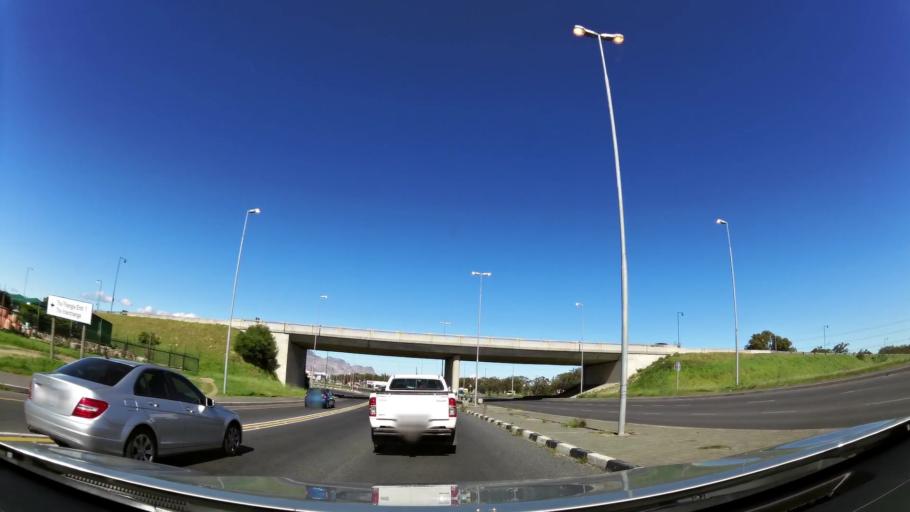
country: ZA
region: Western Cape
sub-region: Cape Winelands District Municipality
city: Stellenbosch
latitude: -34.0811
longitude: 18.8191
